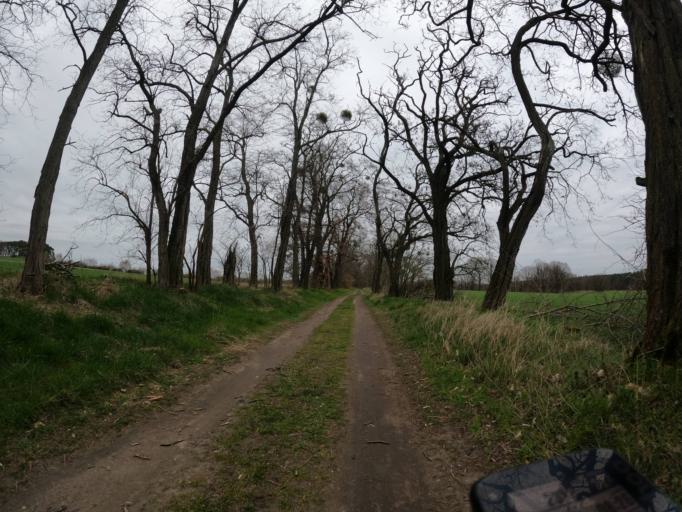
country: DE
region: Brandenburg
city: Werftpfuhl
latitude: 52.5940
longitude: 13.8043
